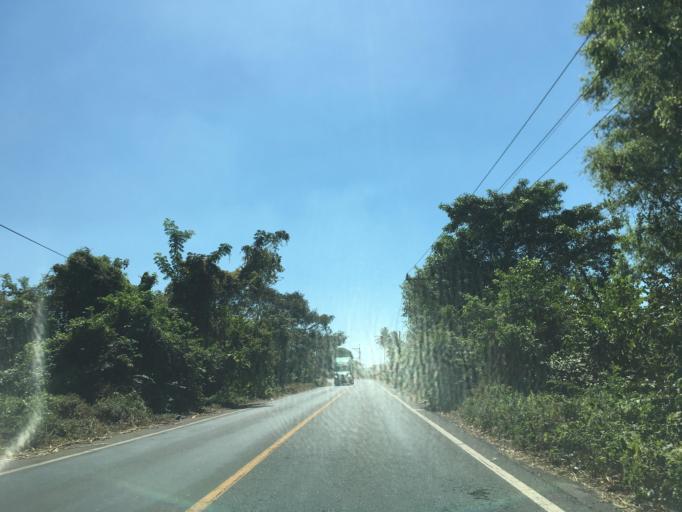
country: GT
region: Escuintla
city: Puerto San Jose
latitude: 13.9808
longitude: -90.8881
